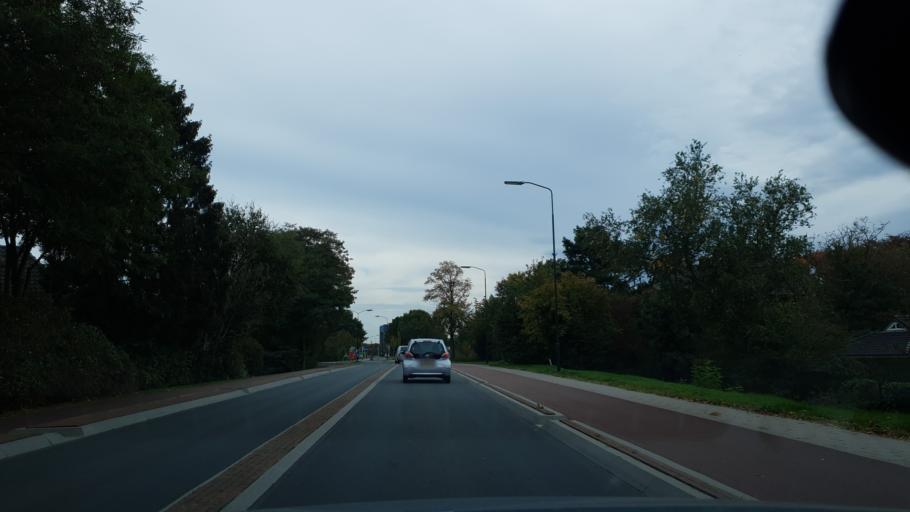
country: NL
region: Gelderland
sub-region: Gemeente Overbetuwe
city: Oosterhout
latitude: 51.8580
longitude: 5.8139
